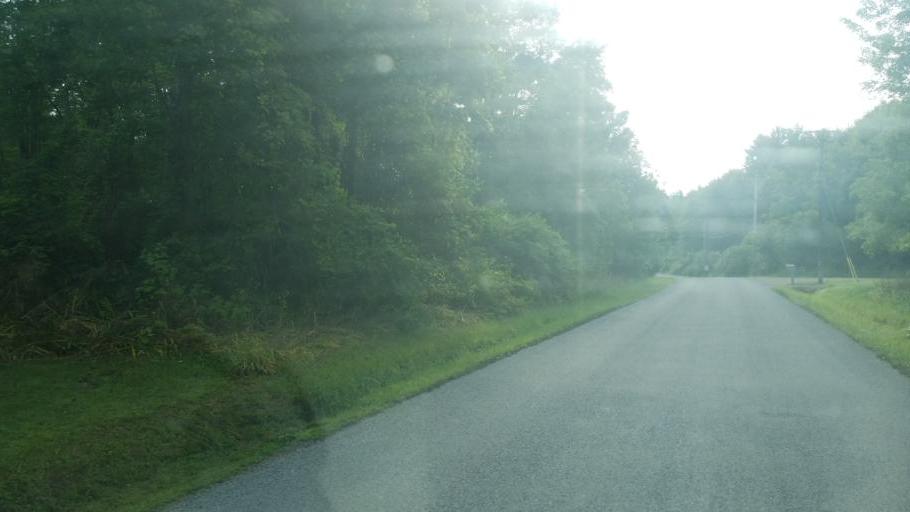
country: US
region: Pennsylvania
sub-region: Crawford County
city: Pymatuning Central
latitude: 41.6194
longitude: -80.4541
